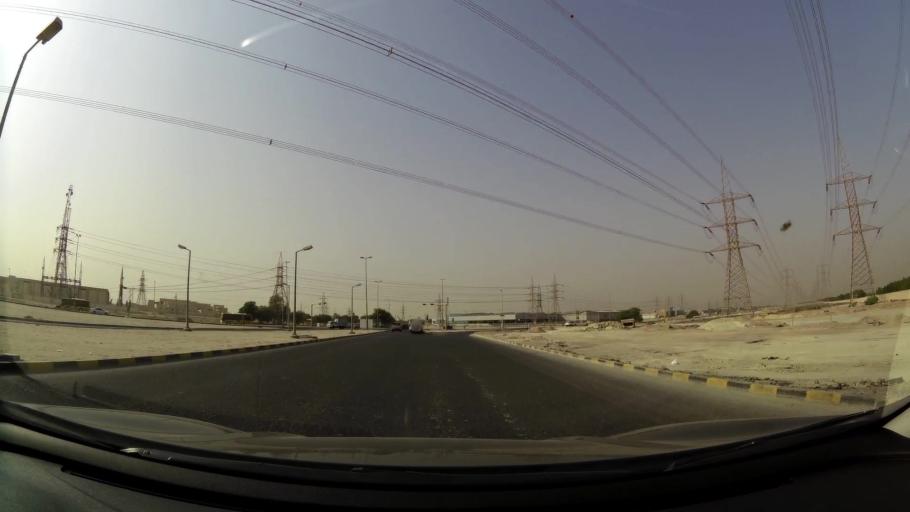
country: KW
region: Al Asimah
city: Ar Rabiyah
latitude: 29.2961
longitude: 47.8534
